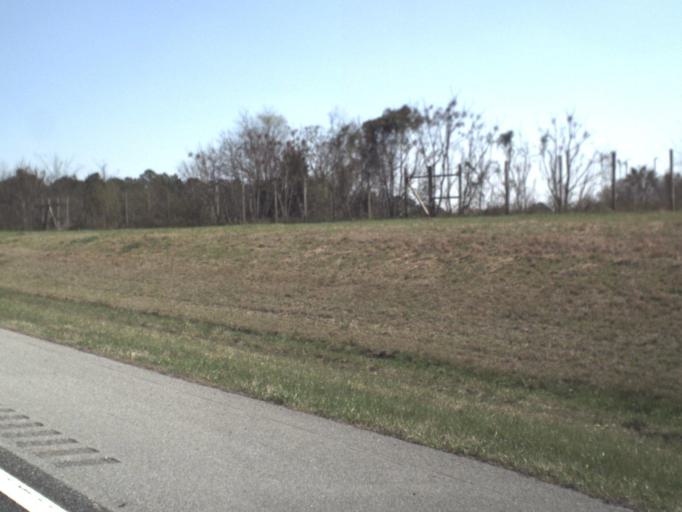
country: US
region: Florida
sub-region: Jackson County
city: Marianna
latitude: 30.7572
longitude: -85.2834
